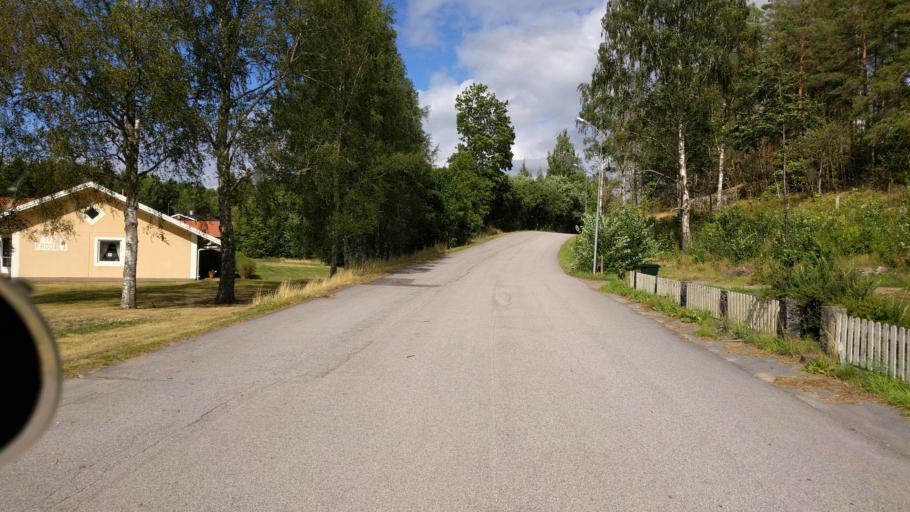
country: SE
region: Kalmar
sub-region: Vimmerby Kommun
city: Vimmerby
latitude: 57.7004
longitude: 16.0044
